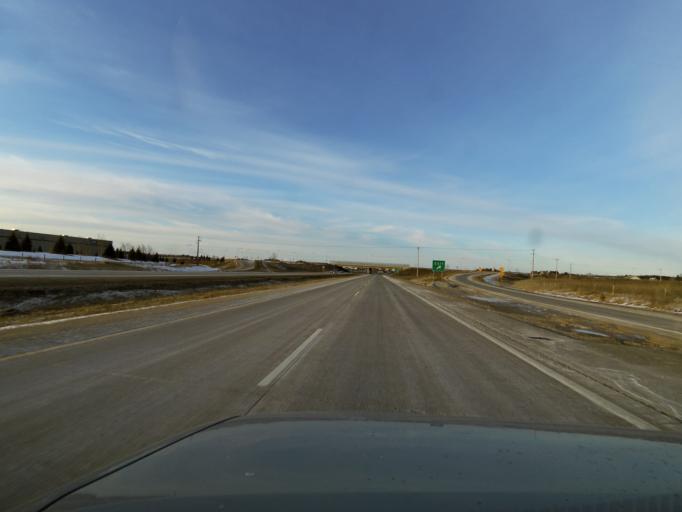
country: US
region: Wisconsin
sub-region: Saint Croix County
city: Hudson
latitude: 44.9459
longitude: -92.6946
